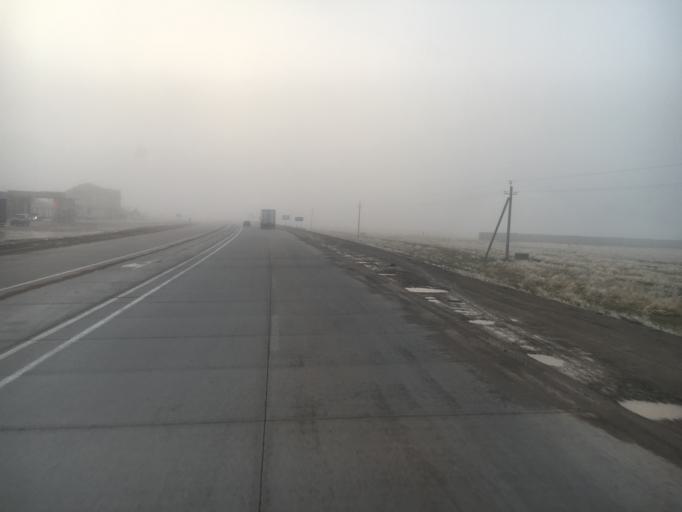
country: KZ
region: Zhambyl
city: Sarykemer
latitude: 43.0034
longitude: 71.6321
